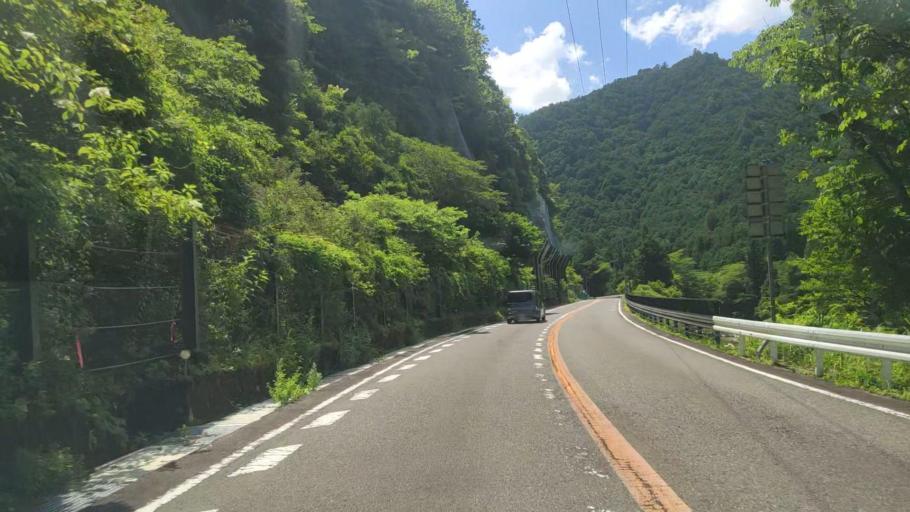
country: JP
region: Mie
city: Owase
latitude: 33.9870
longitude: 136.1101
